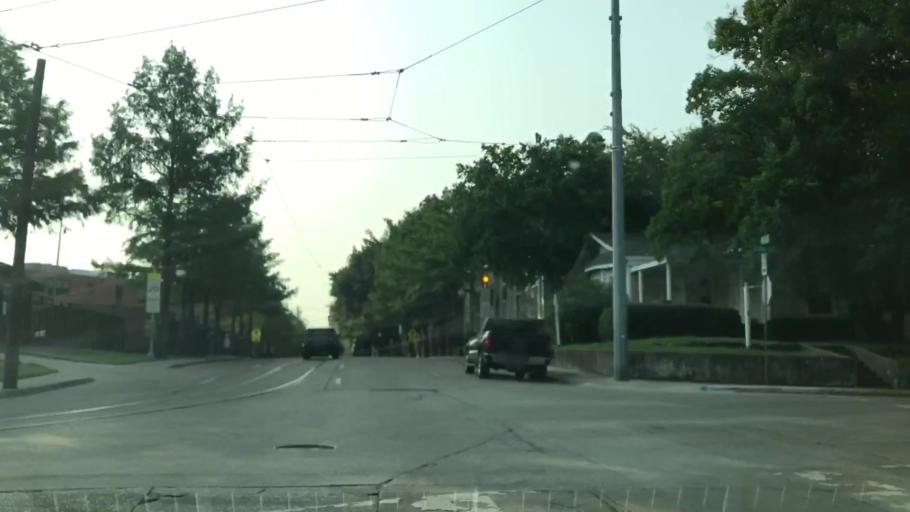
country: US
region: Texas
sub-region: Dallas County
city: Dallas
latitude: 32.8019
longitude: -96.8026
